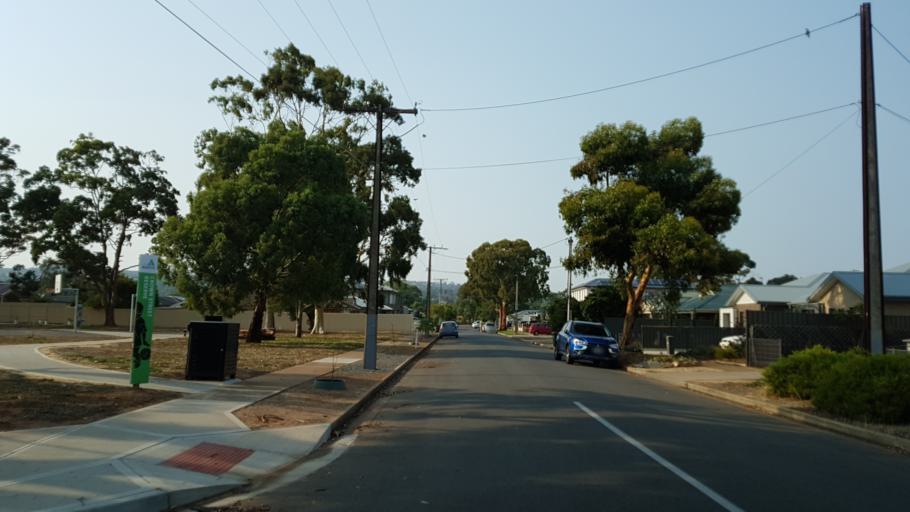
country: AU
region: South Australia
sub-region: Holdfast Bay
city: Seacliff Park
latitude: -35.0203
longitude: 138.5370
